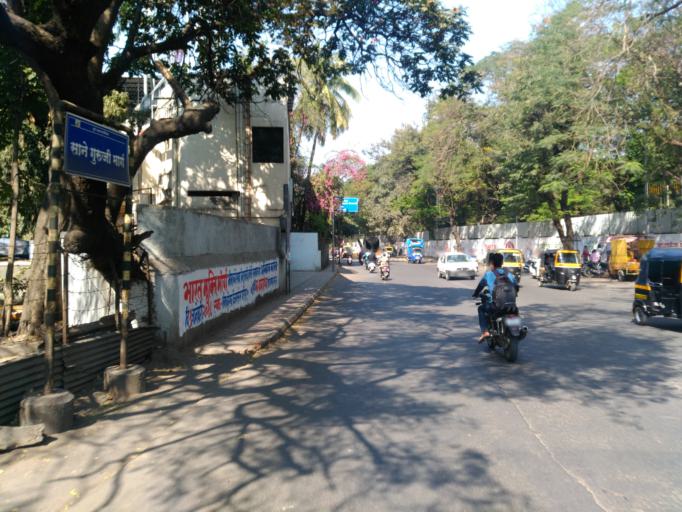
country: IN
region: Maharashtra
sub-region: Pune Division
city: Pune
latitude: 18.5012
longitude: 73.8508
